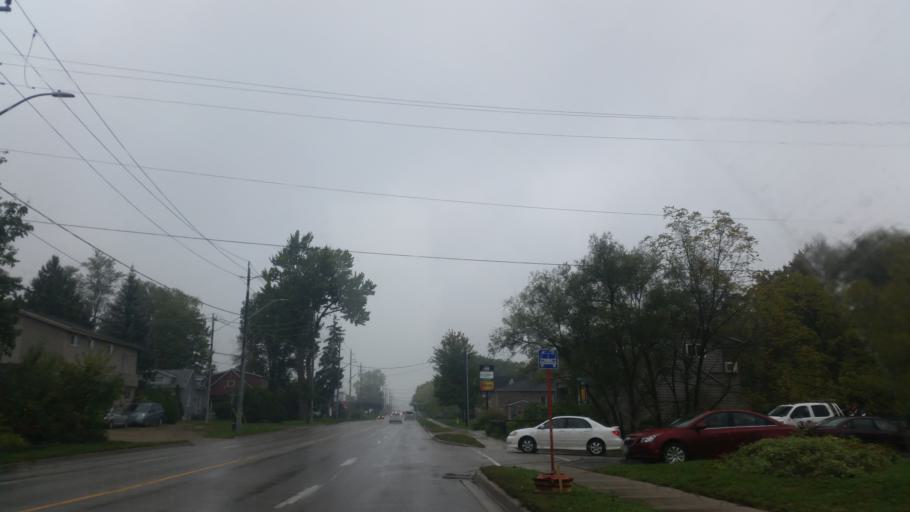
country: CA
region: Ontario
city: Stratford
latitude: 43.3605
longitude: -80.9921
